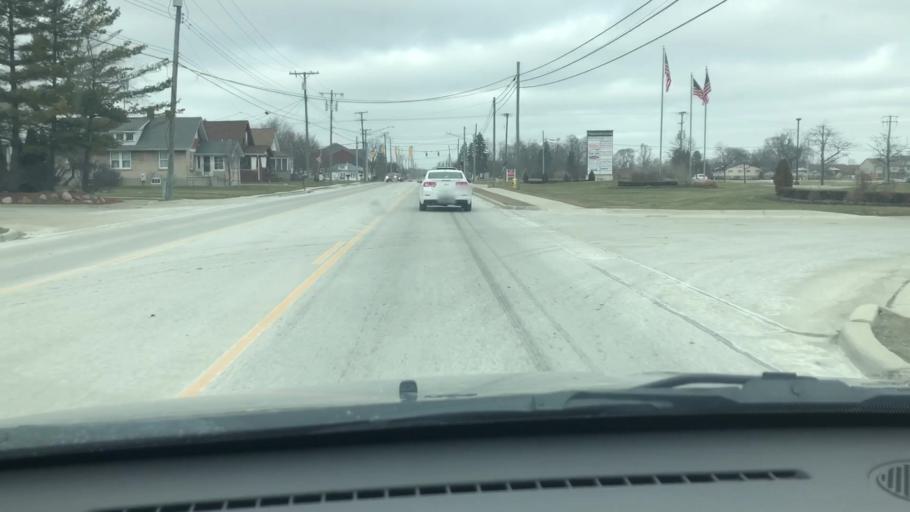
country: US
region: Michigan
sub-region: Macomb County
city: Shelby
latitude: 42.7267
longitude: -83.0357
